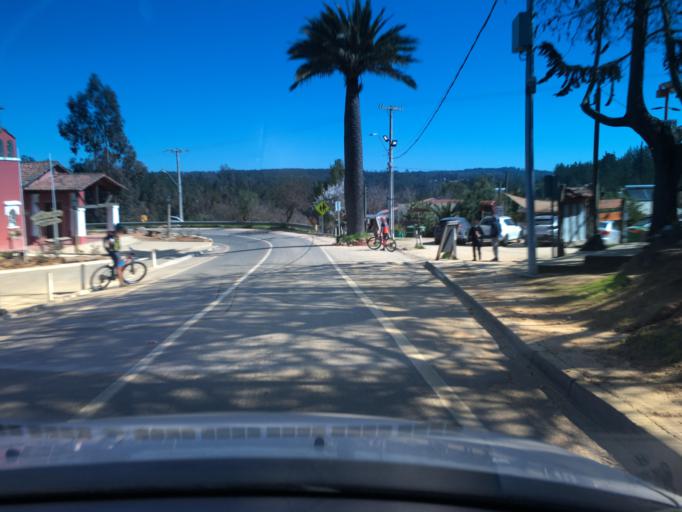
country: CL
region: Valparaiso
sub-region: San Antonio Province
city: El Tabo
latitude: -33.4186
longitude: -71.6247
